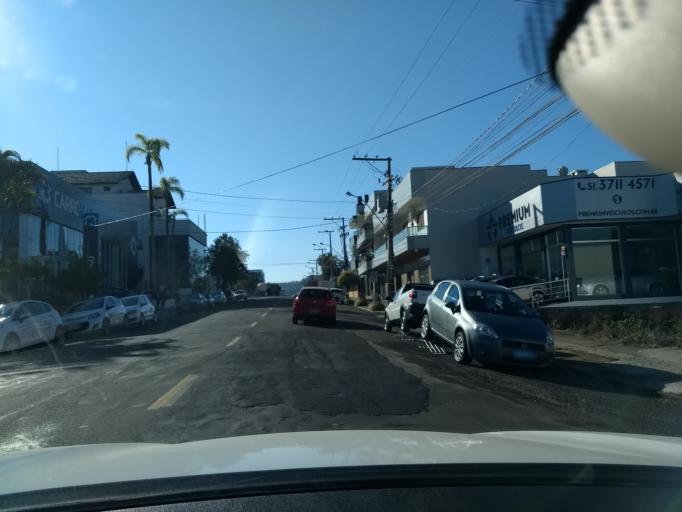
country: BR
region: Rio Grande do Sul
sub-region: Santa Cruz Do Sul
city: Santa Cruz do Sul
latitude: -29.7161
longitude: -52.4403
